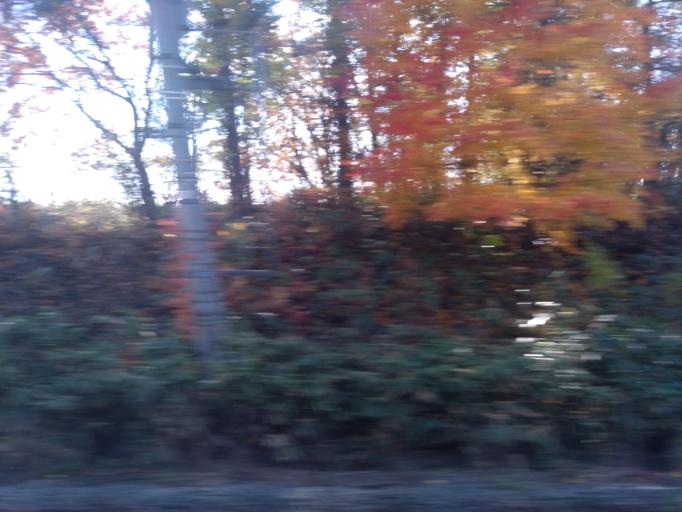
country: JP
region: Hokkaido
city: Kitahiroshima
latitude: 42.9941
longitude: 141.5498
